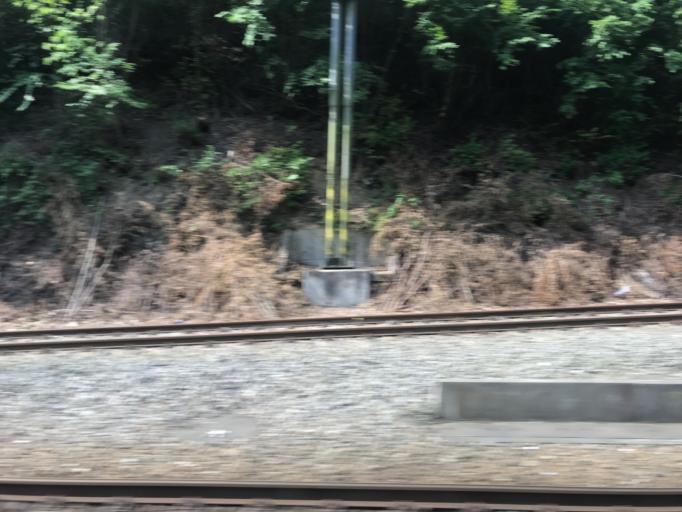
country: CZ
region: Central Bohemia
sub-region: Okres Praha-Vychod
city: Strancice
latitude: 49.9507
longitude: 14.6712
